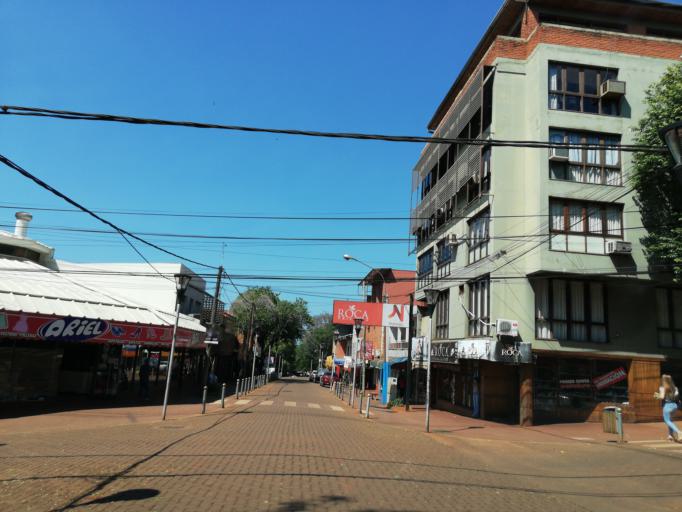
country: AR
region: Misiones
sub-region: Departamento de Eldorado
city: Eldorado
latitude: -26.4098
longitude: -54.6062
